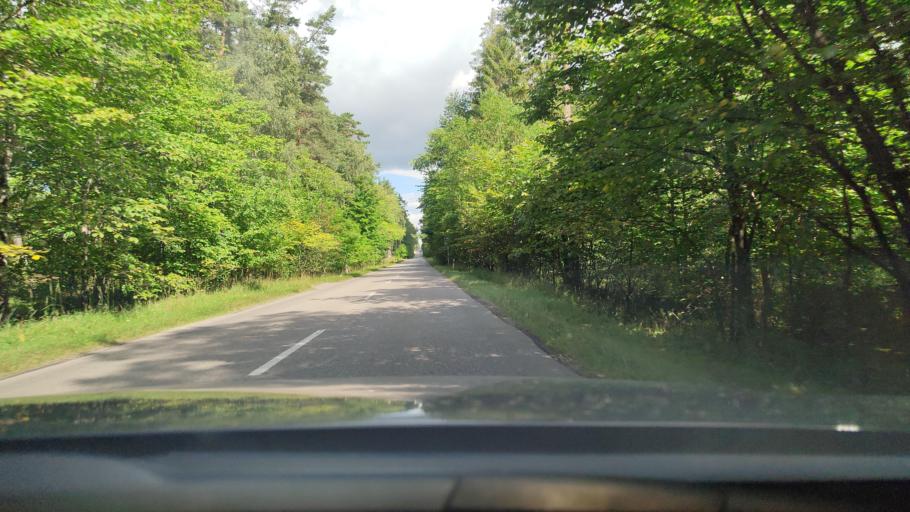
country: PL
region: Pomeranian Voivodeship
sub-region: Powiat wejherowski
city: Orle
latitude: 54.6505
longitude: 18.2120
